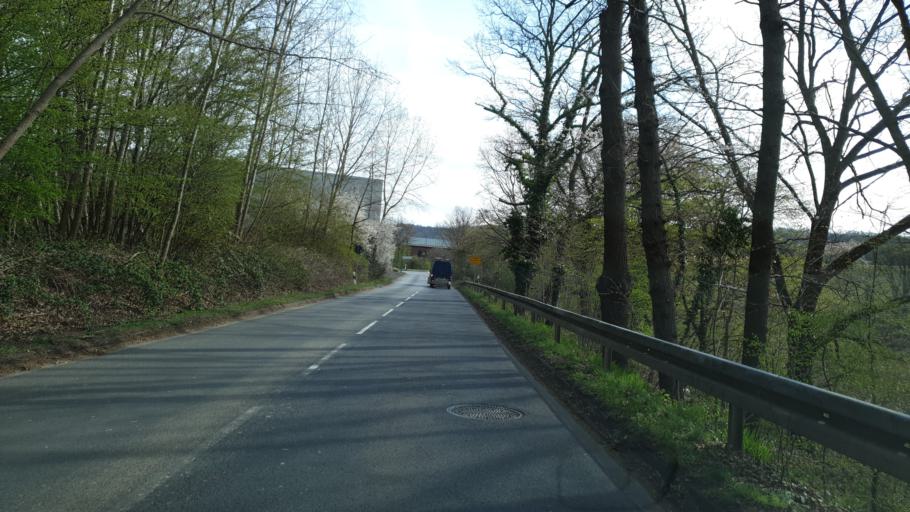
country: DE
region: North Rhine-Westphalia
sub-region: Regierungsbezirk Koln
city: Kerpen
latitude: 50.9197
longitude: 6.7201
